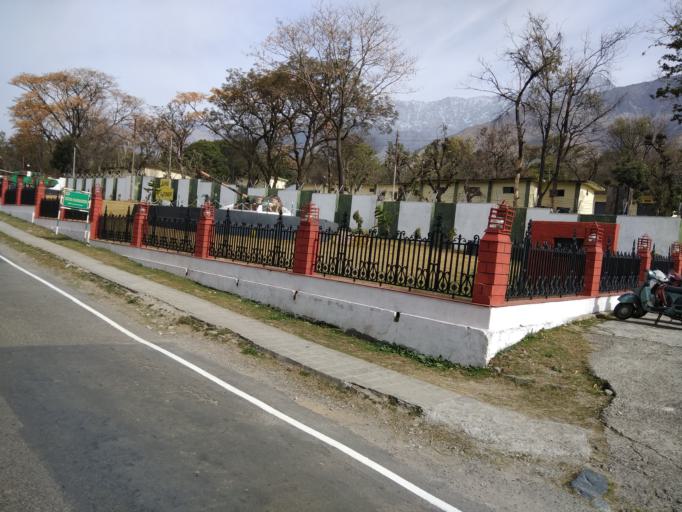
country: IN
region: Himachal Pradesh
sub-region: Kangra
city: Dharmsala
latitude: 32.1766
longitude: 76.3808
